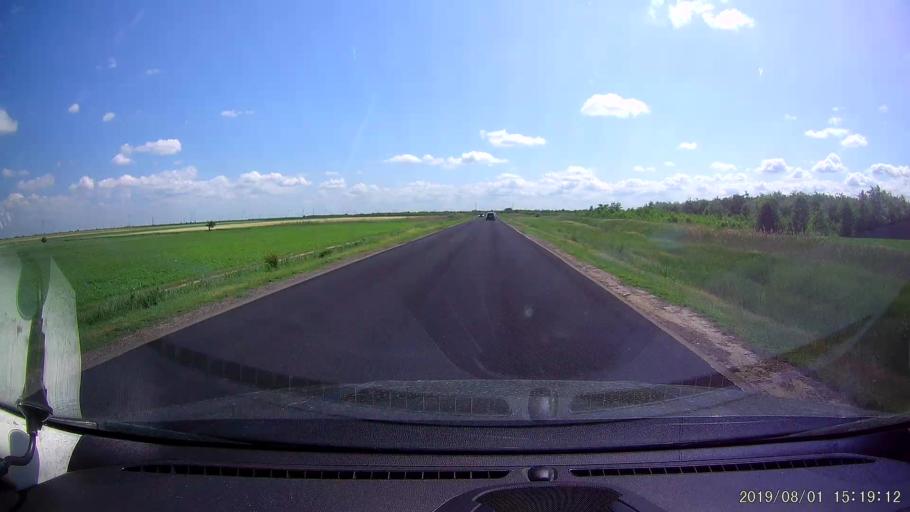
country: RO
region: Braila
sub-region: Comuna Unirea
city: Unirea
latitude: 45.0930
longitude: 27.8144
